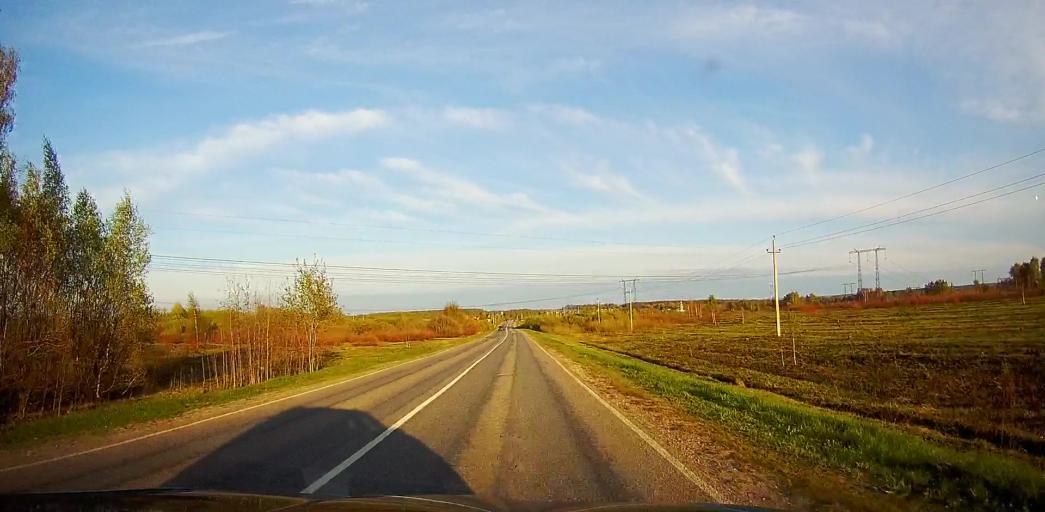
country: RU
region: Moskovskaya
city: Meshcherino
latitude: 55.2644
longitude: 38.2572
